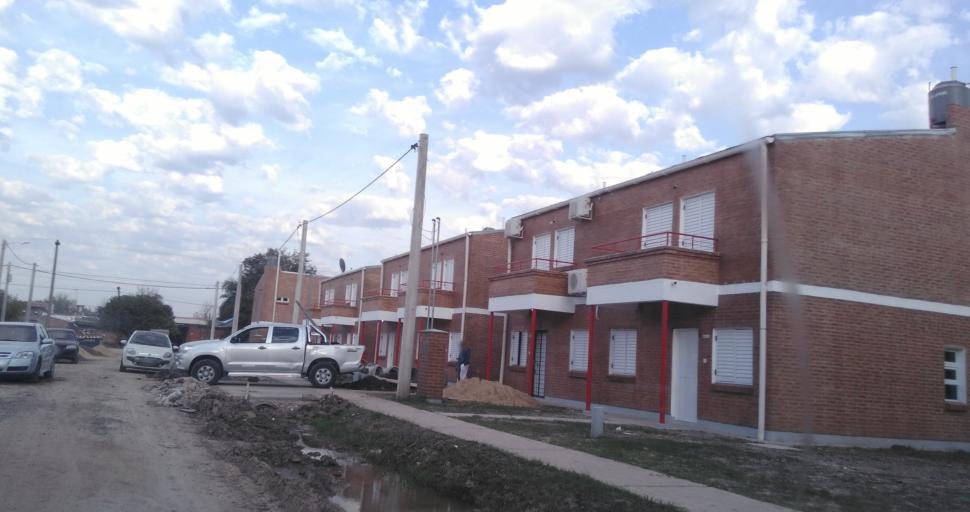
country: AR
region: Chaco
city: Fontana
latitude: -27.4427
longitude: -59.0289
